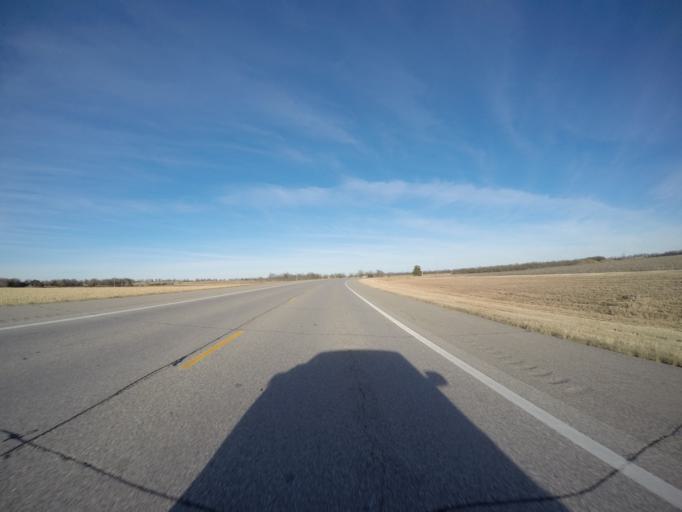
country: US
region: Kansas
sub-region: Marion County
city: Peabody
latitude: 38.1732
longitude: -97.1921
